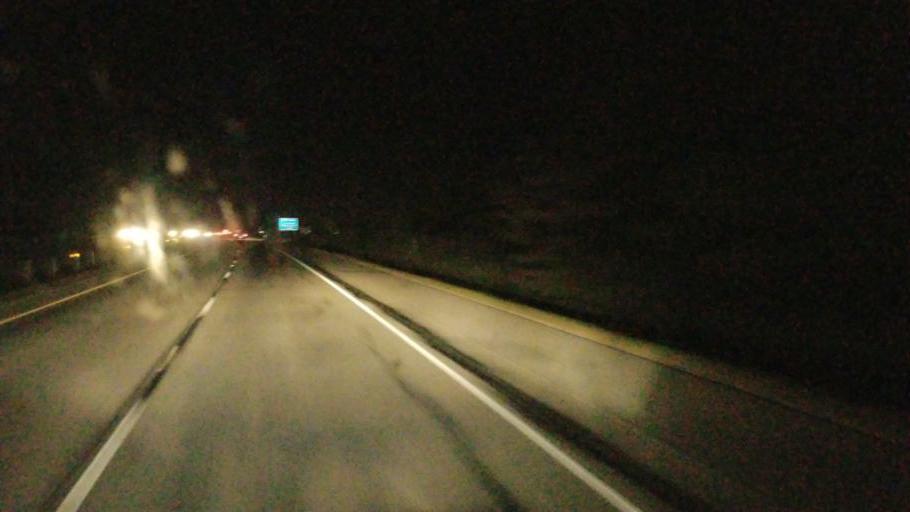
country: US
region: Indiana
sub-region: Allen County
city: Leo-Cedarville
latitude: 41.2602
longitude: -85.0866
